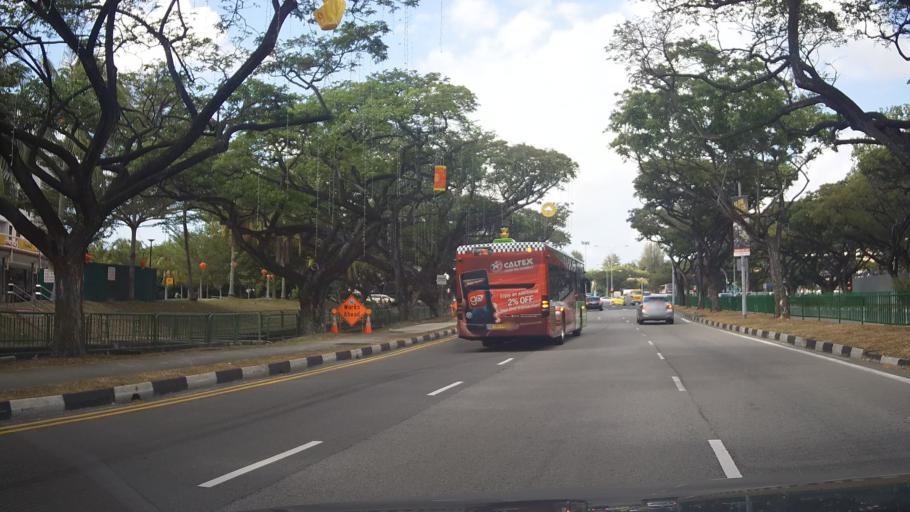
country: SG
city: Singapore
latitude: 1.3472
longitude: 103.9442
